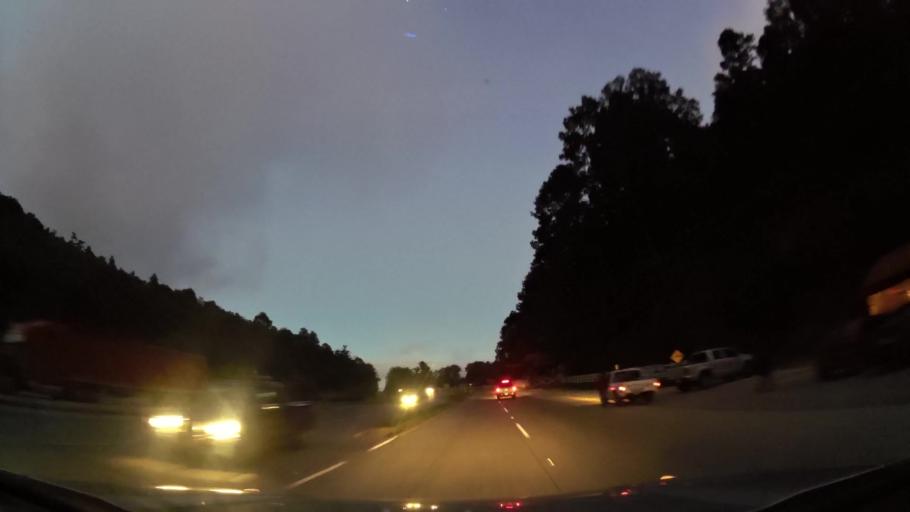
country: GT
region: Chimaltenango
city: Santa Apolonia
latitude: 14.7978
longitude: -90.9822
